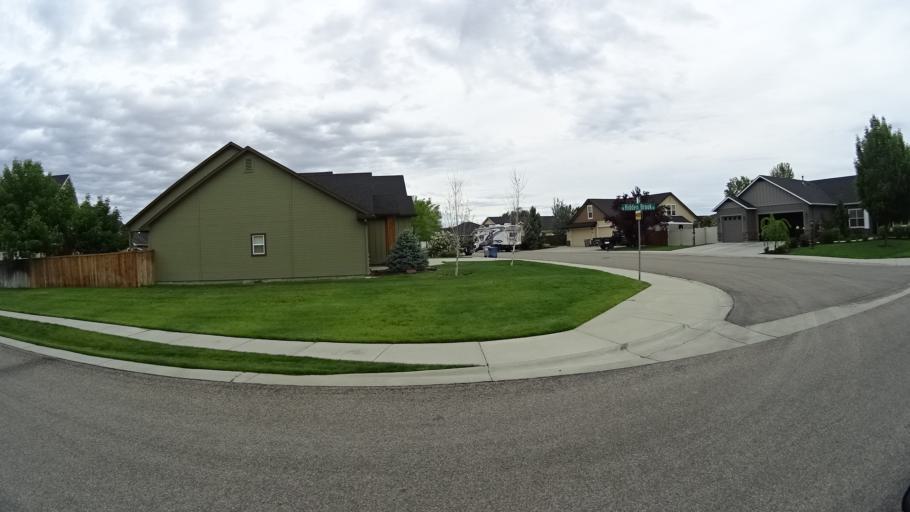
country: US
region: Idaho
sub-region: Ada County
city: Star
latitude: 43.7004
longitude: -116.4883
